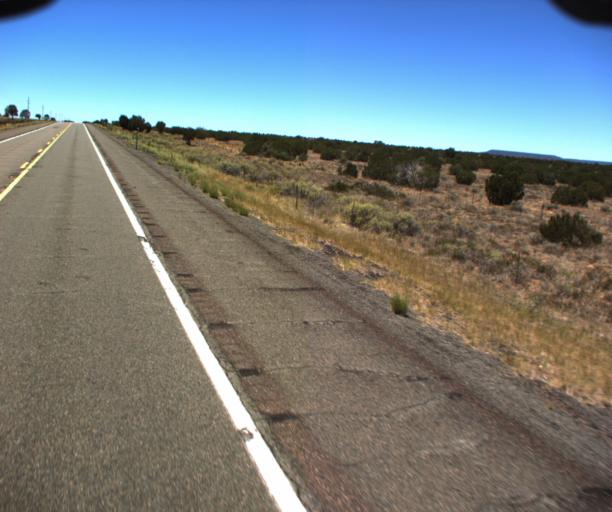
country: US
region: Arizona
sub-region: Coconino County
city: LeChee
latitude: 34.8026
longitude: -110.9793
